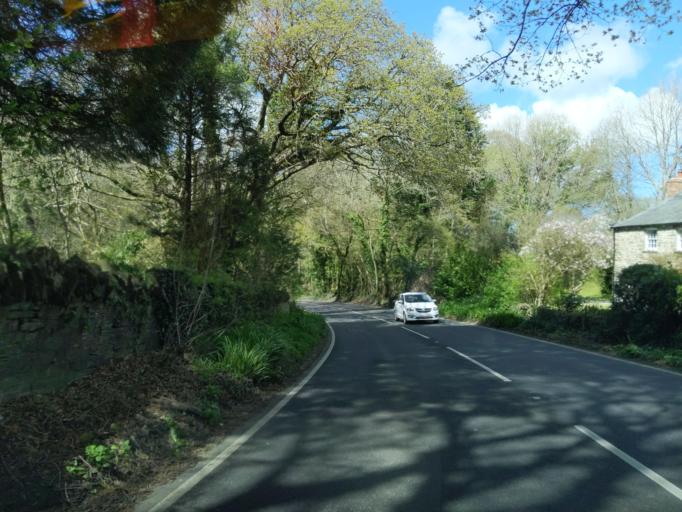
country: GB
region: England
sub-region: Cornwall
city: Bodmin
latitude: 50.4998
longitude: -4.7753
